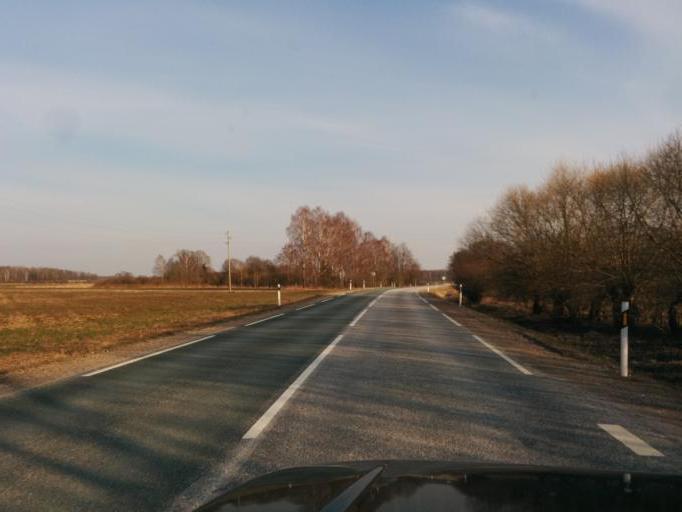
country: LV
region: Lecava
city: Iecava
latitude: 56.5939
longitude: 24.1286
